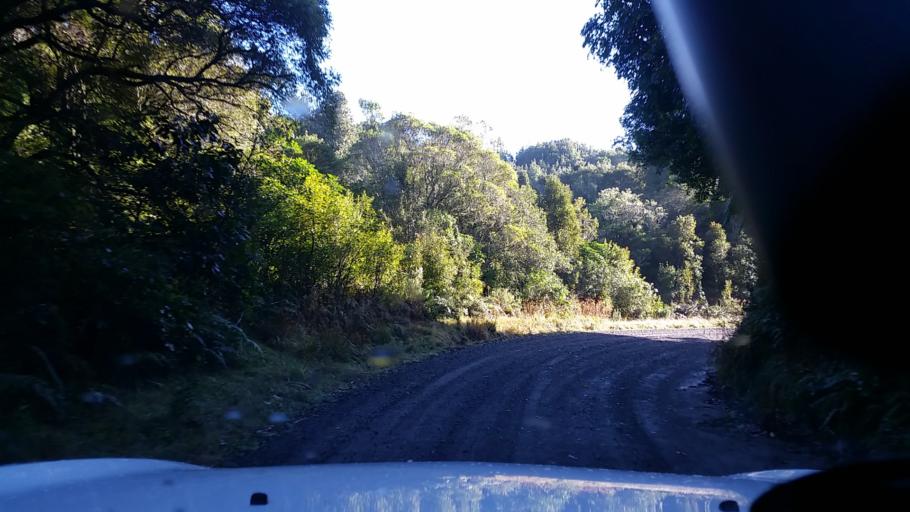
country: NZ
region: Bay of Plenty
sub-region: Kawerau District
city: Kawerau
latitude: -38.0039
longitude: 176.5971
